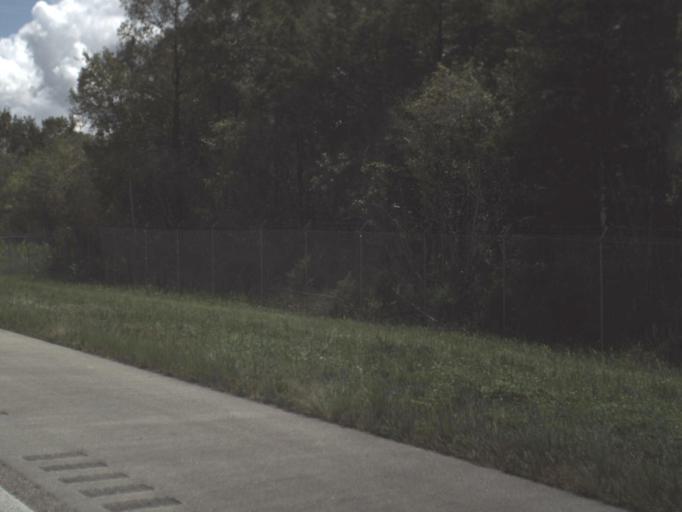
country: US
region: Florida
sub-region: Collier County
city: Orangetree
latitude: 26.1539
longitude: -81.3873
